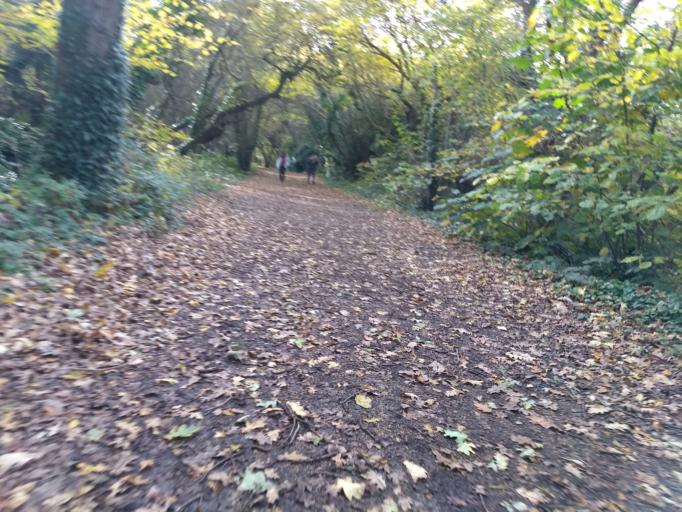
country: GB
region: England
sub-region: Isle of Wight
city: Freshwater
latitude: 50.6927
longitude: -1.5011
